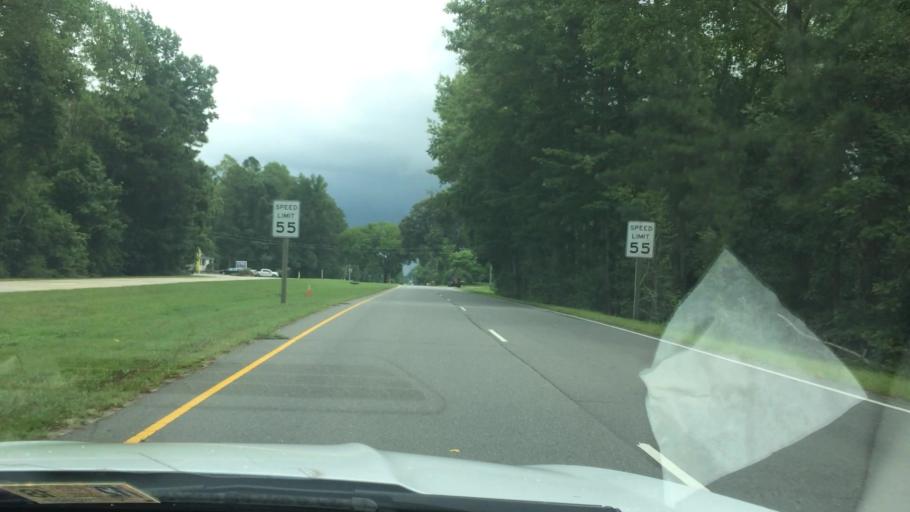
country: US
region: Virginia
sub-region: King William County
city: West Point
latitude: 37.4041
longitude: -76.8385
